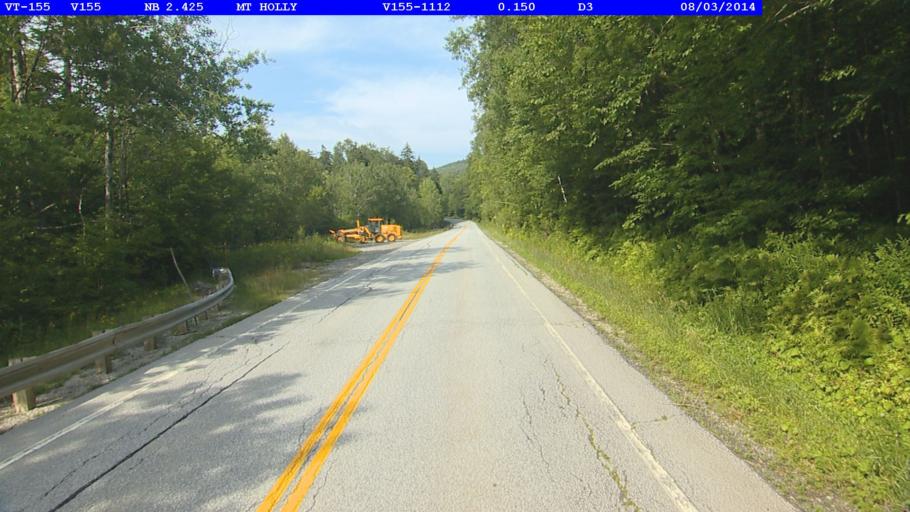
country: US
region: Vermont
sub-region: Windsor County
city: Chester
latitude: 43.3693
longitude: -72.7901
